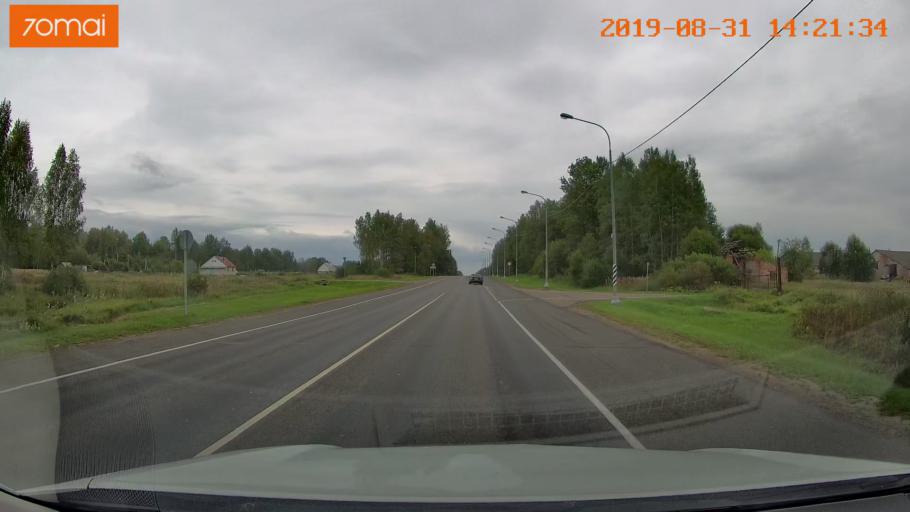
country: RU
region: Smolensk
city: Yekimovichi
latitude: 54.0863
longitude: 33.2000
